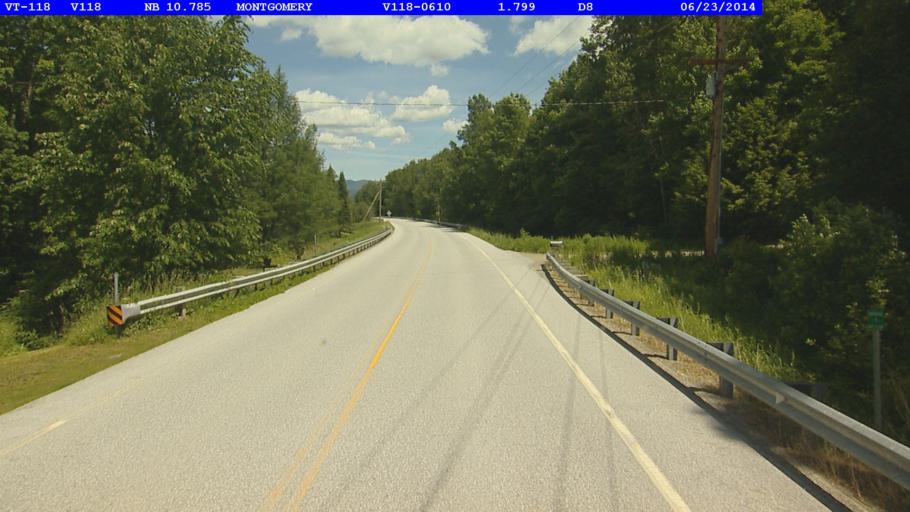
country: US
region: Vermont
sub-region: Franklin County
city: Richford
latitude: 44.8240
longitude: -72.6099
